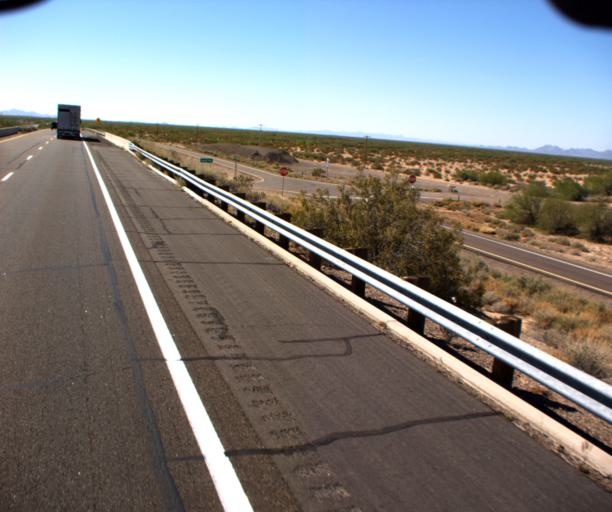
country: US
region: Arizona
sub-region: Maricopa County
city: Gila Bend
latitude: 32.8359
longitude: -113.3567
